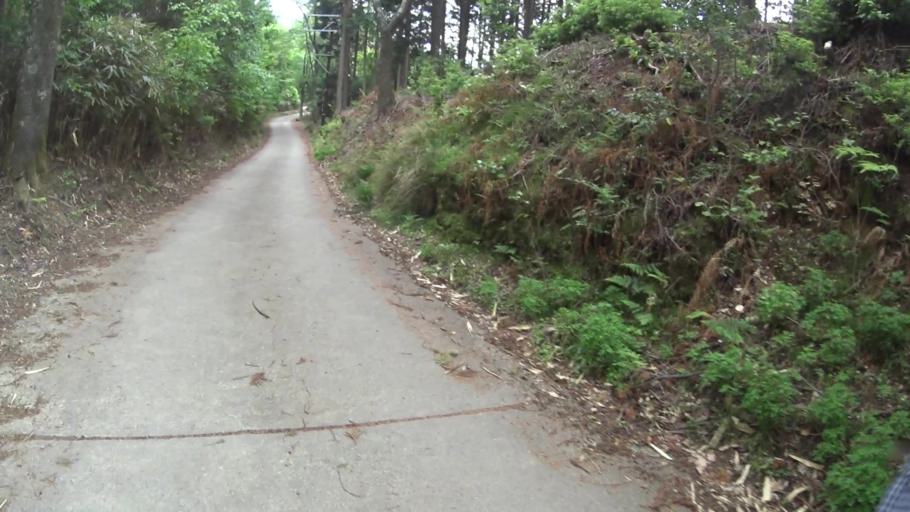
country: JP
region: Nara
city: Yoshino-cho
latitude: 34.3471
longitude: 135.8789
